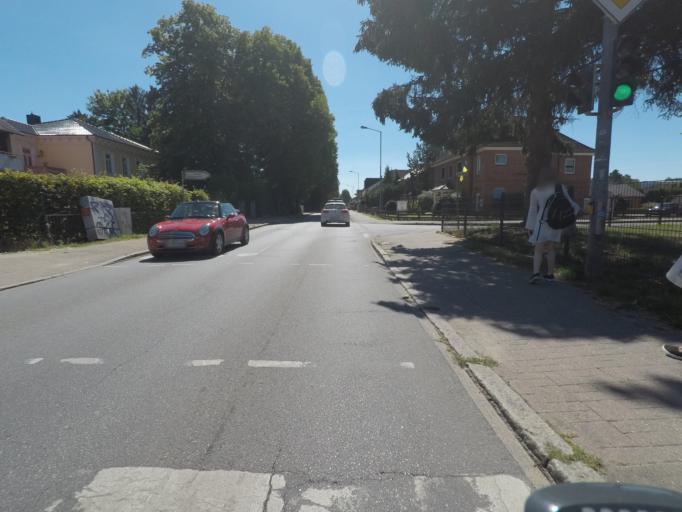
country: DE
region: Schleswig-Holstein
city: Trittau
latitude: 53.6194
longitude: 10.4029
